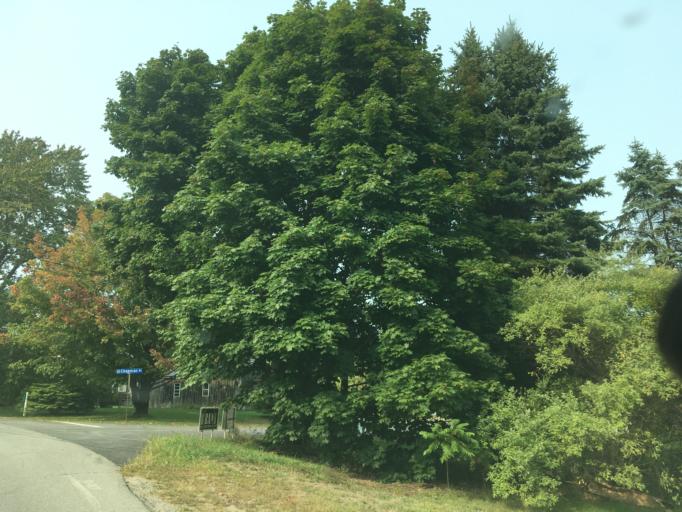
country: US
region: New Hampshire
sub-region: Rockingham County
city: North Hampton
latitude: 42.9924
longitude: -70.8846
